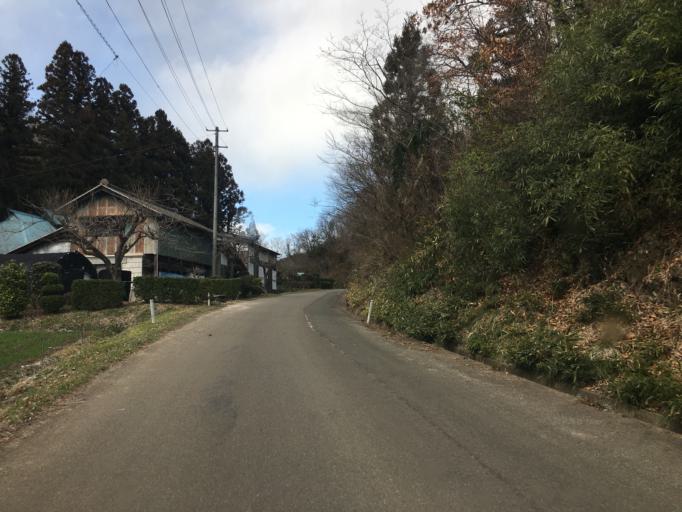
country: JP
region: Fukushima
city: Yanagawamachi-saiwaicho
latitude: 37.8337
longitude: 140.6108
